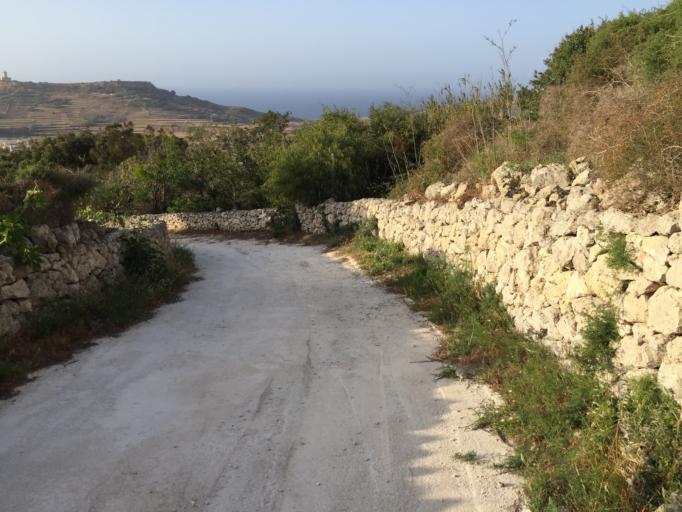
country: MT
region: L-Gharb
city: Gharb
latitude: 36.0602
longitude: 14.2192
